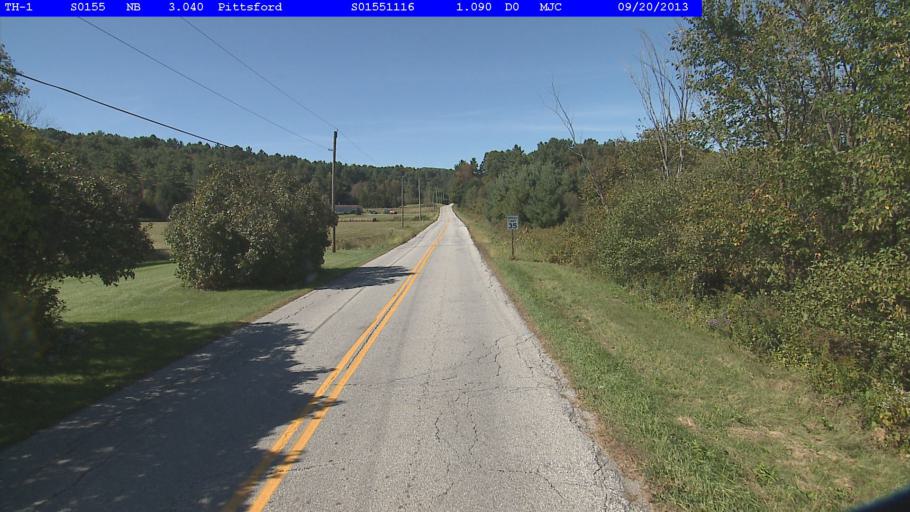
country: US
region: Vermont
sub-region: Rutland County
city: Brandon
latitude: 43.7061
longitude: -73.0502
